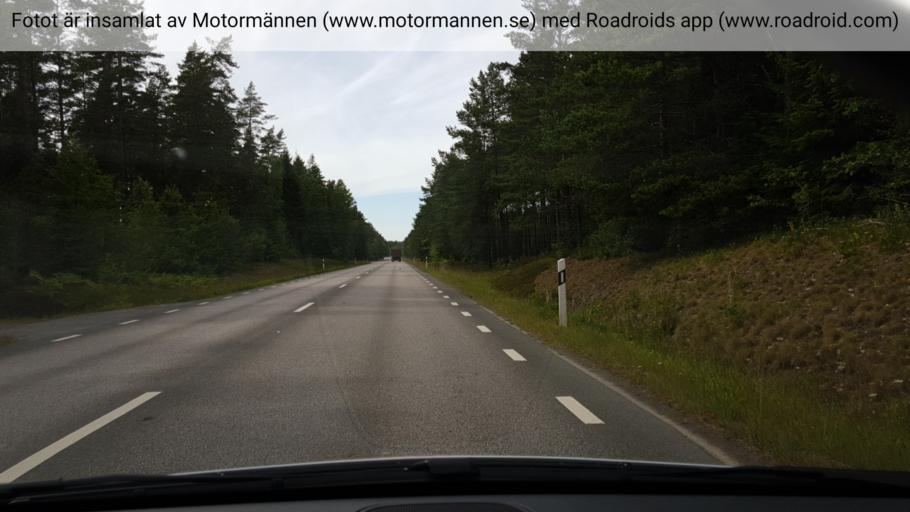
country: SE
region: Vaestra Goetaland
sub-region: Hjo Kommun
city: Hjo
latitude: 58.3369
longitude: 14.2428
